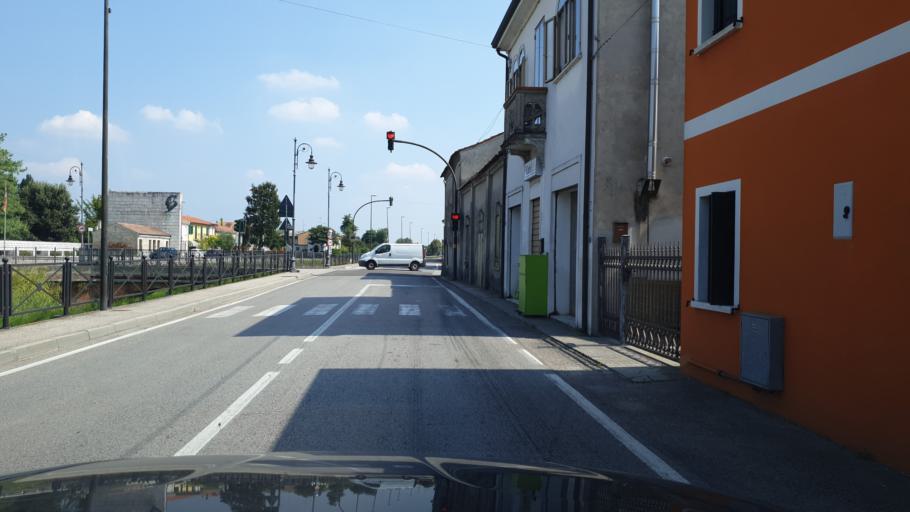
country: IT
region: Veneto
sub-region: Provincia di Rovigo
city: Villamarzana
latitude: 45.0145
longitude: 11.6928
